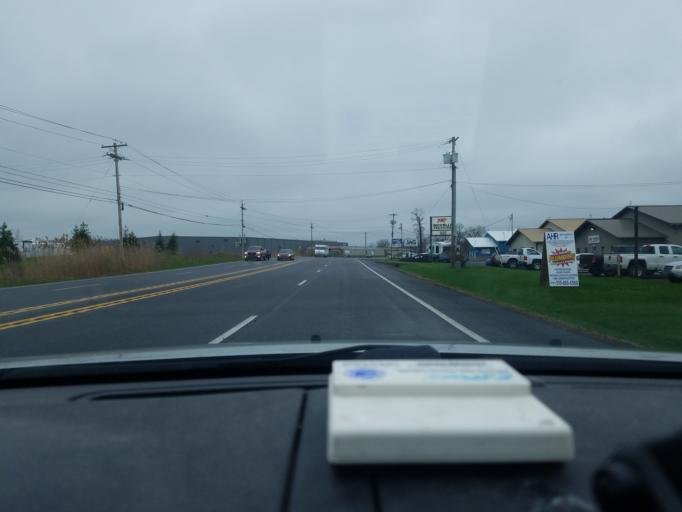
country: US
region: New York
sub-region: Onondaga County
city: North Syracuse
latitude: 43.1252
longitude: -76.0923
